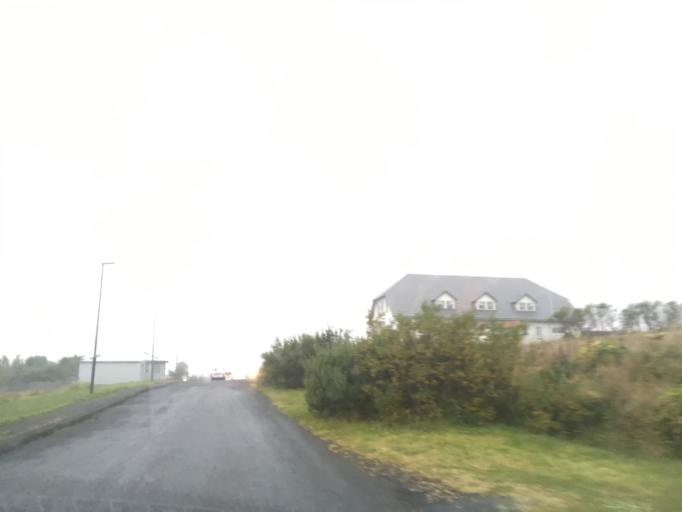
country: IS
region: South
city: Vestmannaeyjar
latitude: 63.4211
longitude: -19.0123
